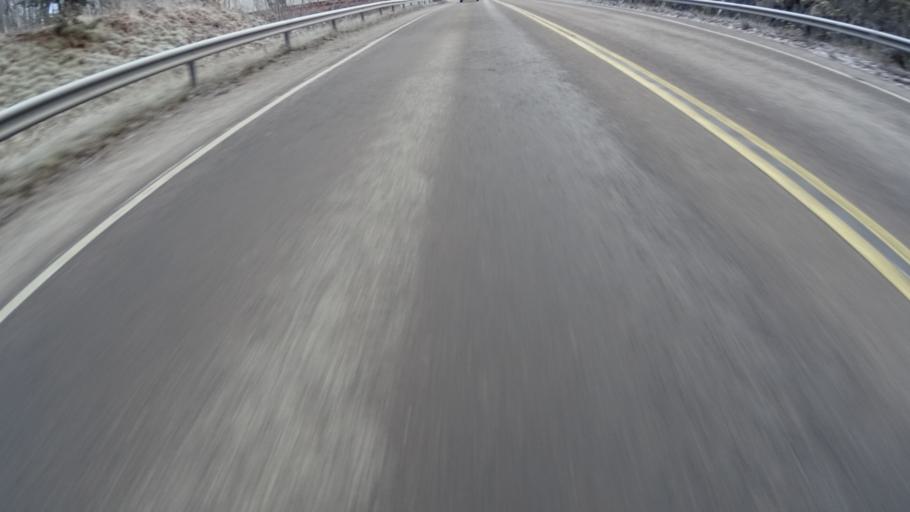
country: FI
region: Uusimaa
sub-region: Helsinki
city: Nurmijaervi
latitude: 60.4307
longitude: 24.7216
